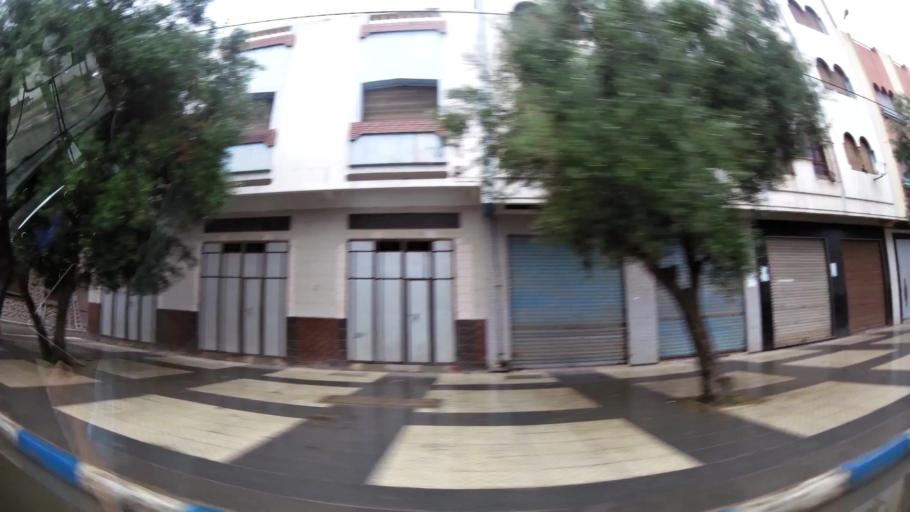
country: MA
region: Oriental
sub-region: Nador
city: Nador
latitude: 35.1641
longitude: -2.9585
